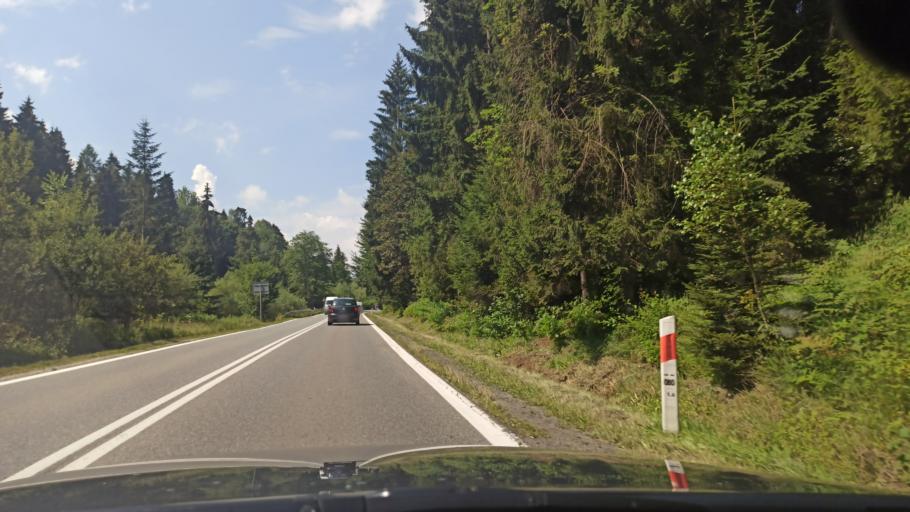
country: PL
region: Lesser Poland Voivodeship
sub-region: Powiat nowotarski
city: Krosnica
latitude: 49.4422
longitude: 20.3523
